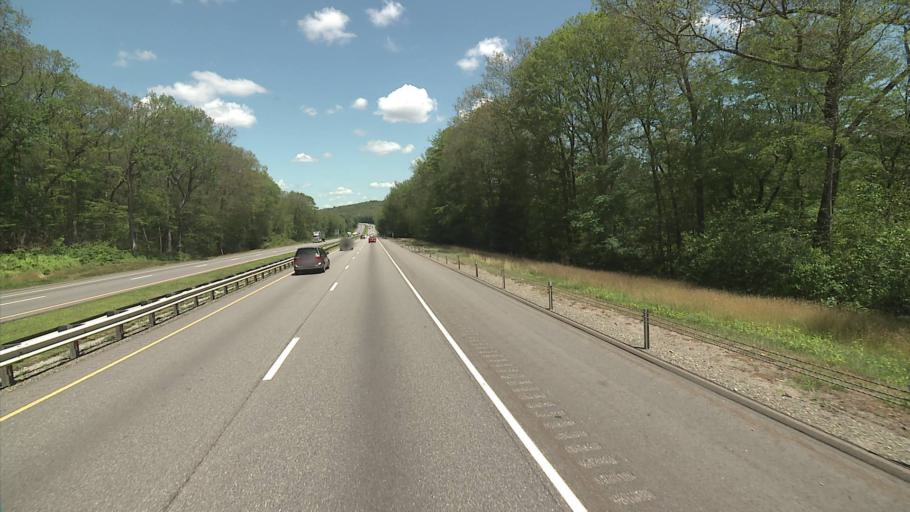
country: US
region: Connecticut
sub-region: New London County
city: Oxoboxo River
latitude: 41.4521
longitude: -72.1168
